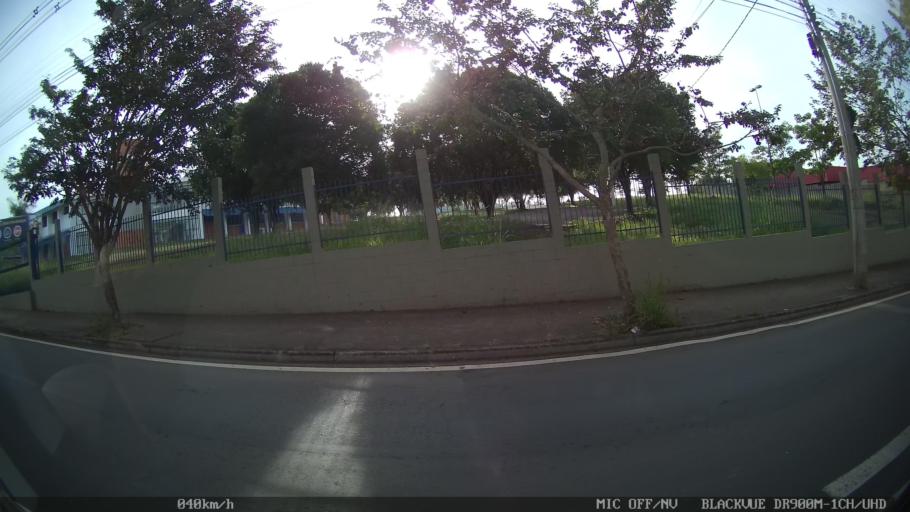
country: BR
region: Sao Paulo
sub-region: Piracicaba
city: Piracicaba
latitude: -22.7020
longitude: -47.6512
